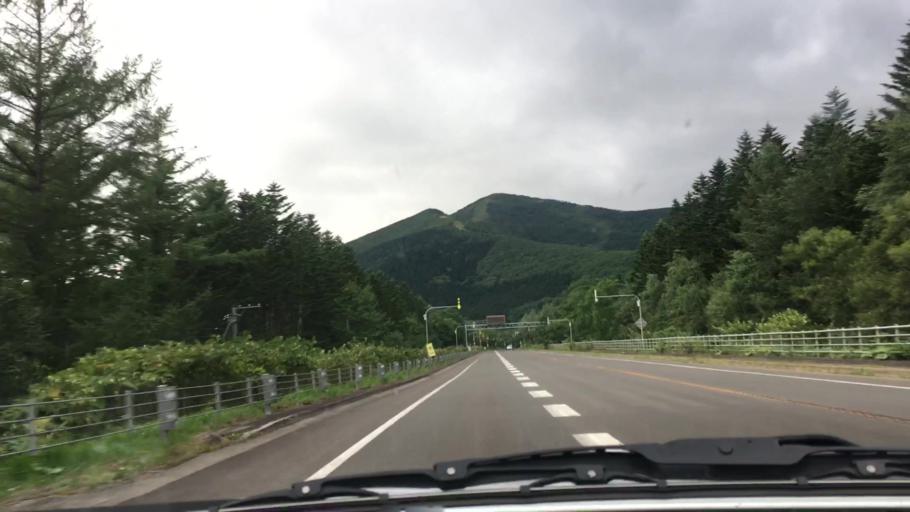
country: JP
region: Hokkaido
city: Otofuke
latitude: 43.1611
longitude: 142.8162
